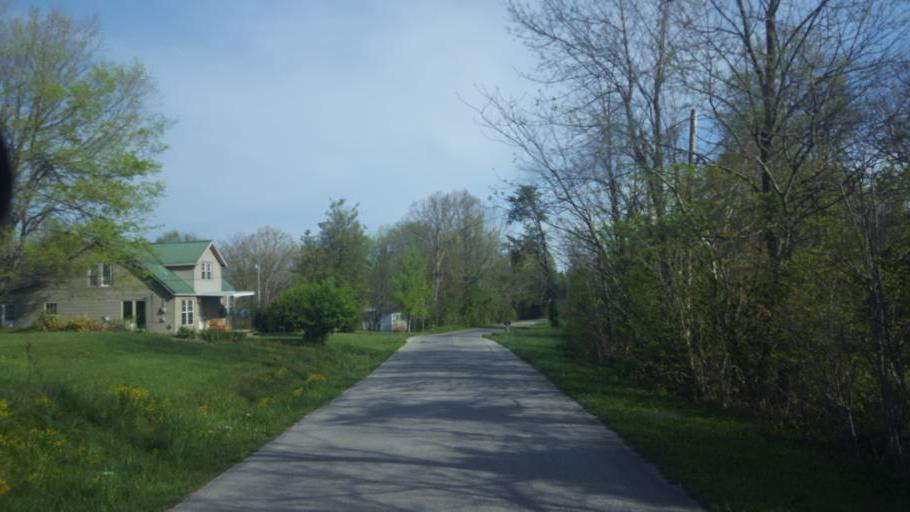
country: US
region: Kentucky
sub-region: Hart County
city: Munfordville
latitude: 37.3247
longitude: -86.0958
